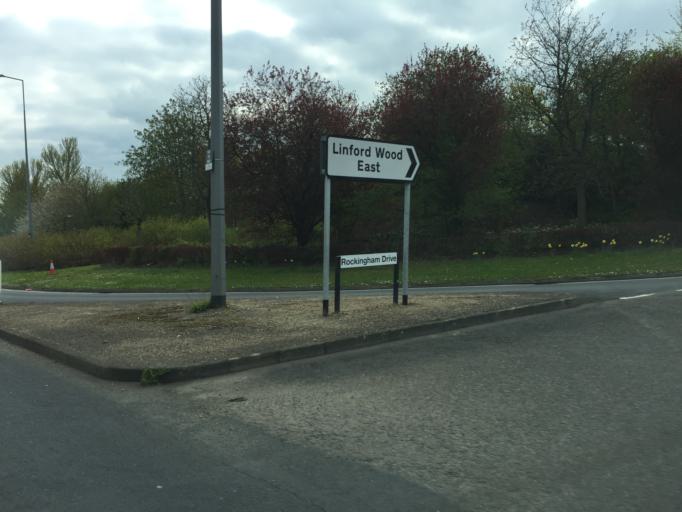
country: GB
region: England
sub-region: Milton Keynes
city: Milton Keynes
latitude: 52.0572
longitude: -0.7548
